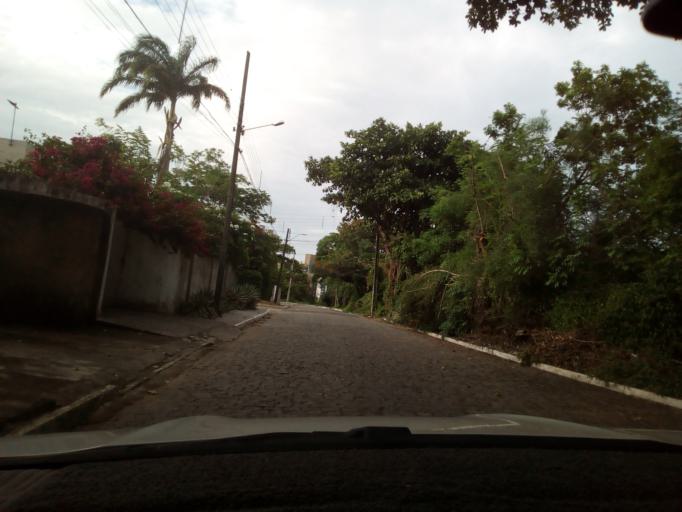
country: BR
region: Paraiba
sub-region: Joao Pessoa
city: Joao Pessoa
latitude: -7.1139
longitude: -34.8360
